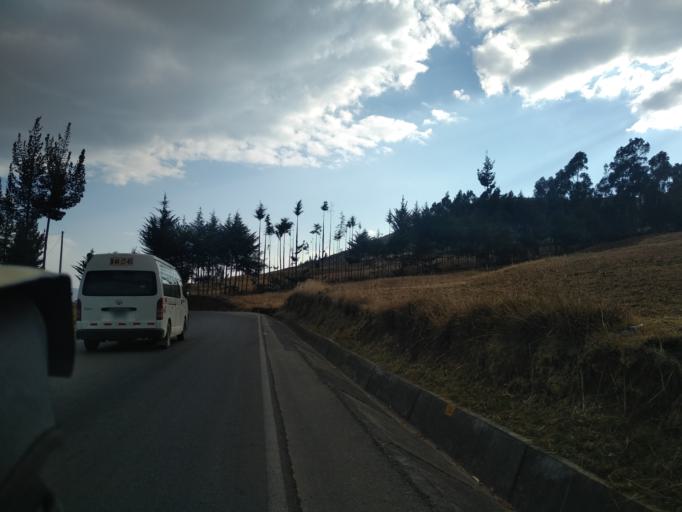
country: PE
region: Cajamarca
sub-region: Provincia de Cajamarca
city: Llacanora
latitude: -7.1472
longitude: -78.4103
